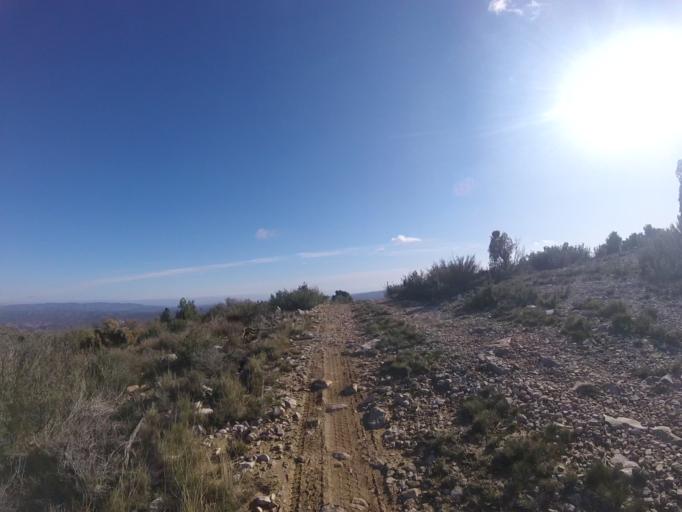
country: ES
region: Valencia
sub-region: Provincia de Castello
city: Sarratella
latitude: 40.3007
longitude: 0.0414
